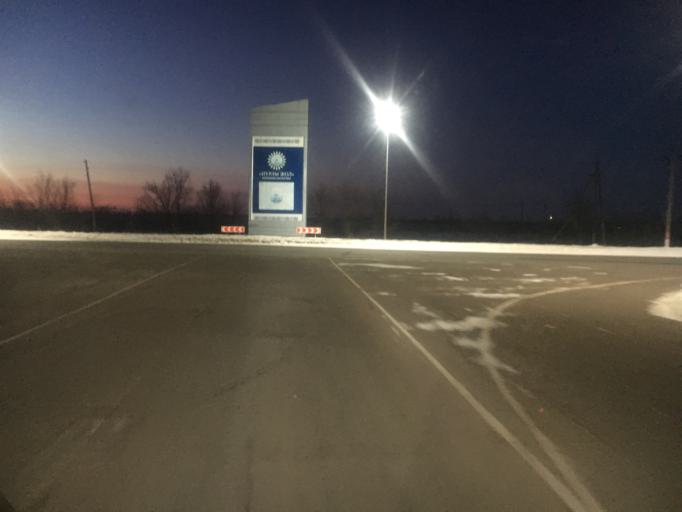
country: KZ
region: Batys Qazaqstan
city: Oral
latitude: 51.1653
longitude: 51.5240
